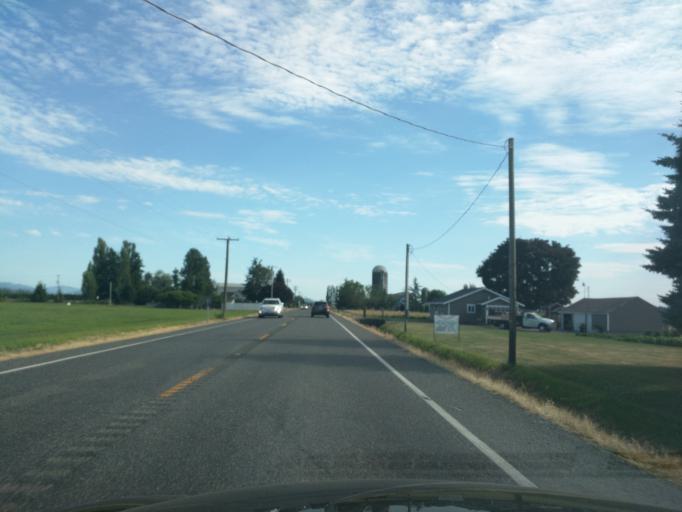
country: US
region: Washington
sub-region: Whatcom County
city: Lynden
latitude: 48.9879
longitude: -122.4852
